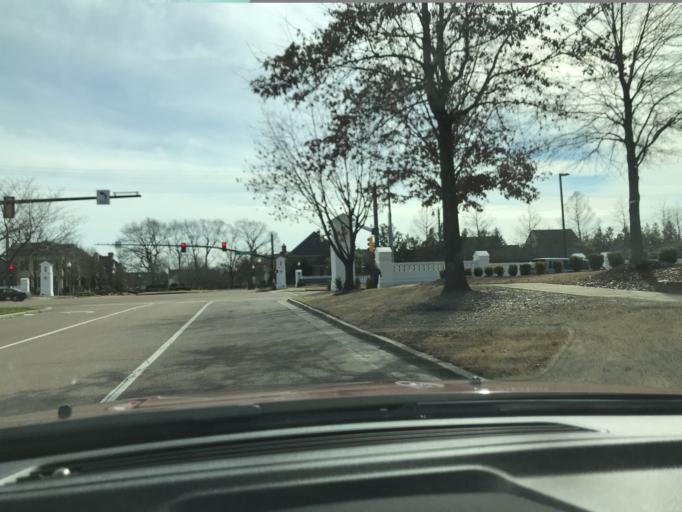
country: US
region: Tennessee
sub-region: Shelby County
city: Collierville
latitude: 35.0385
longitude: -89.7033
